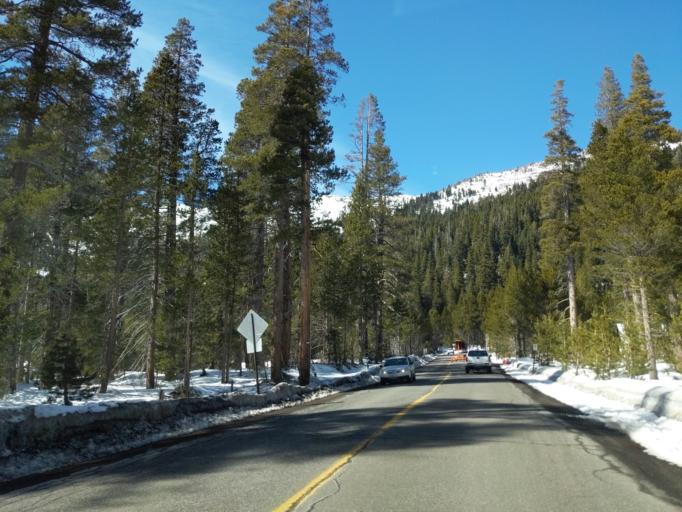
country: US
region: California
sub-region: El Dorado County
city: South Lake Tahoe
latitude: 38.8180
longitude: -120.0745
